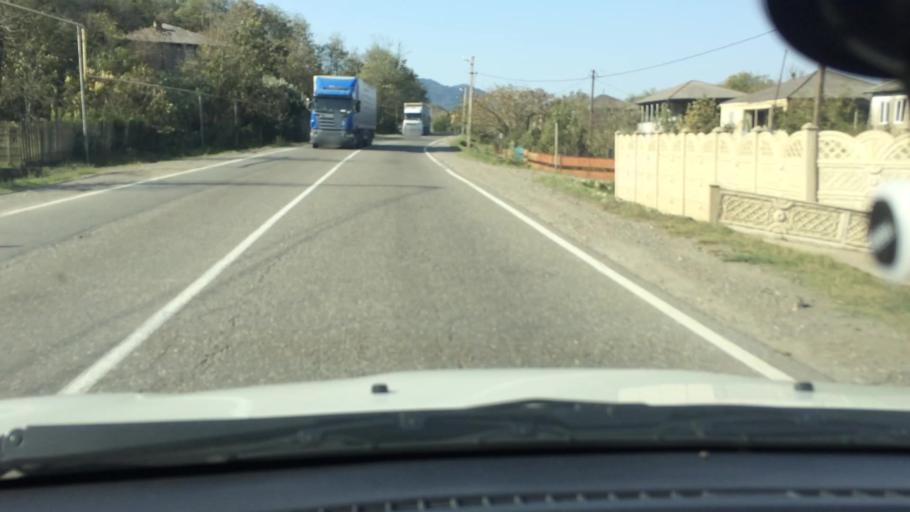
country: GE
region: Guria
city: Lanchkhuti
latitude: 42.0856
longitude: 42.1169
